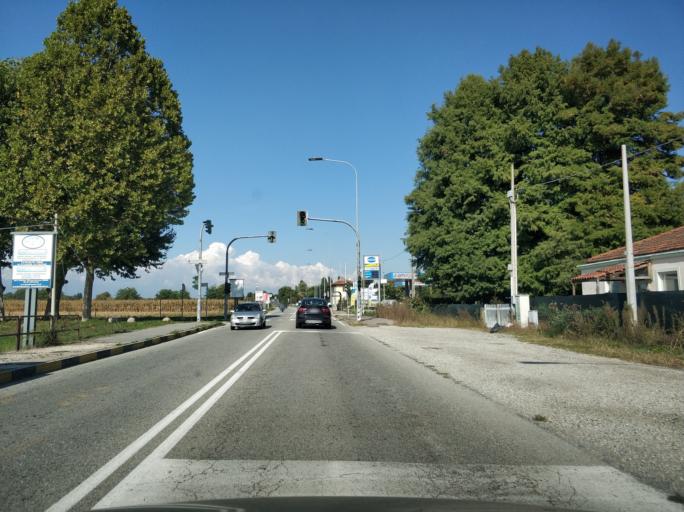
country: IT
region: Piedmont
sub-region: Provincia di Torino
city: Borgaro Torinese
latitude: 45.1253
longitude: 7.7037
